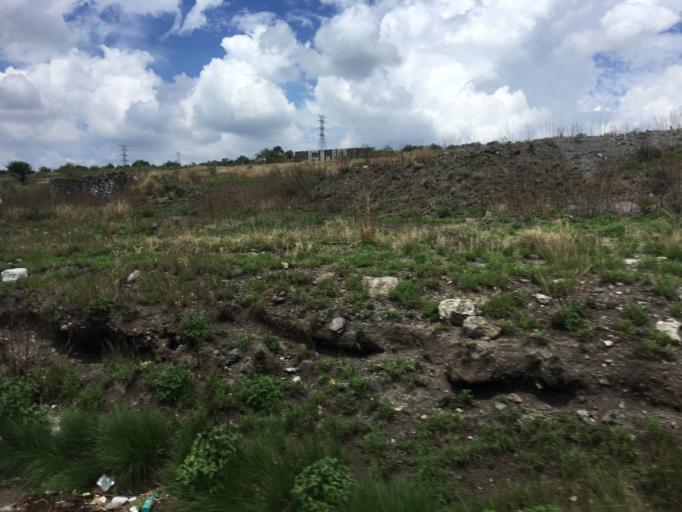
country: MX
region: Guanajuato
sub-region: Irapuato
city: Ex-Hacienda del Copal
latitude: 20.7403
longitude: -101.3411
